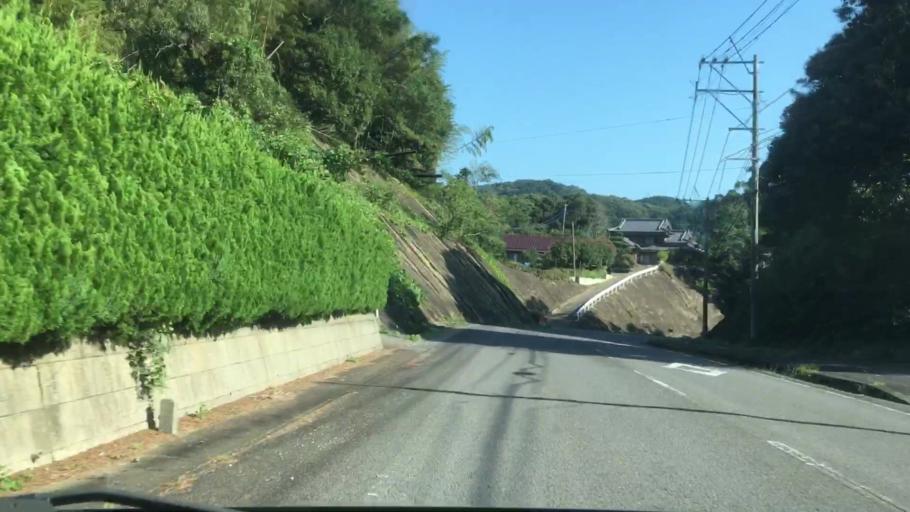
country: JP
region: Nagasaki
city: Sasebo
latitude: 32.9984
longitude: 129.6591
